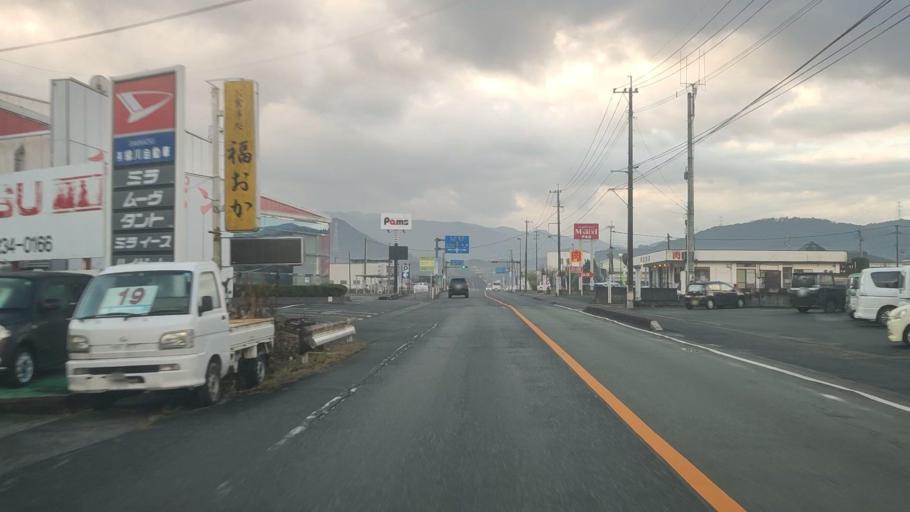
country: JP
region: Kumamoto
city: Matsubase
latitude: 32.6495
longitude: 130.8111
